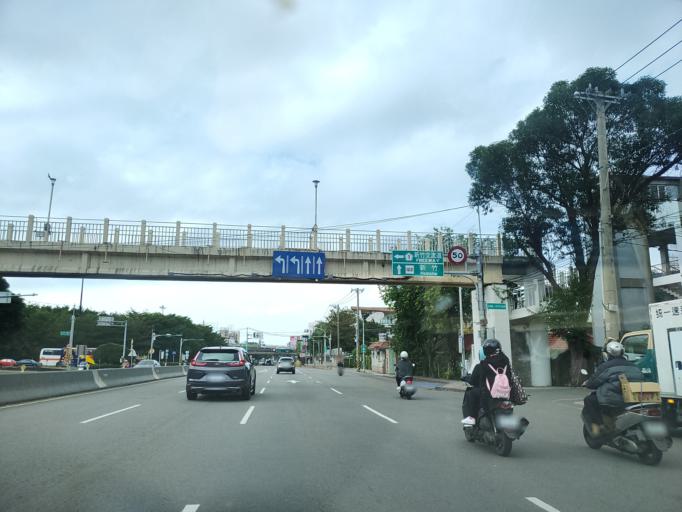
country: TW
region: Taiwan
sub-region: Hsinchu
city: Hsinchu
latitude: 24.7889
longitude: 121.0077
